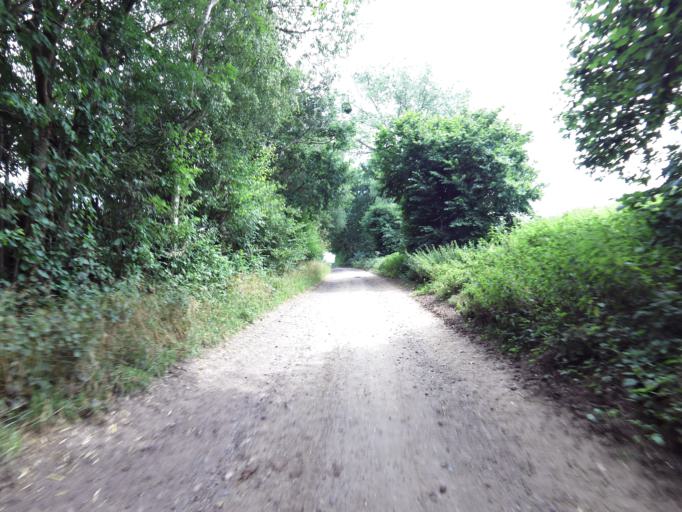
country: NL
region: Limburg
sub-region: Gemeente Simpelveld
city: Simpelveld
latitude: 50.8102
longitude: 5.9862
